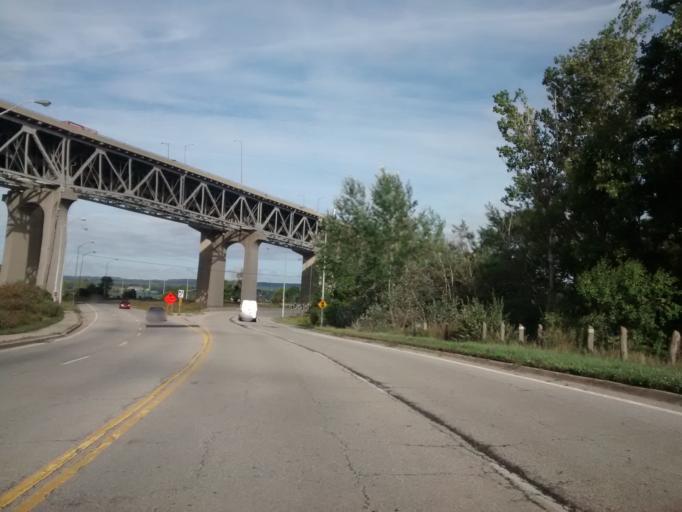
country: CA
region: Ontario
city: Hamilton
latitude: 43.3007
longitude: -79.7968
